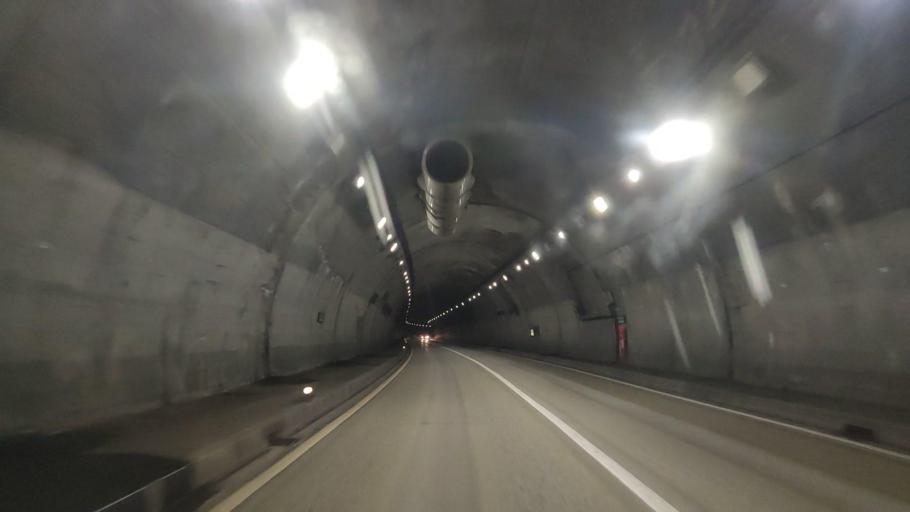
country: JP
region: Nagano
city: Omachi
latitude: 36.5498
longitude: 137.8434
